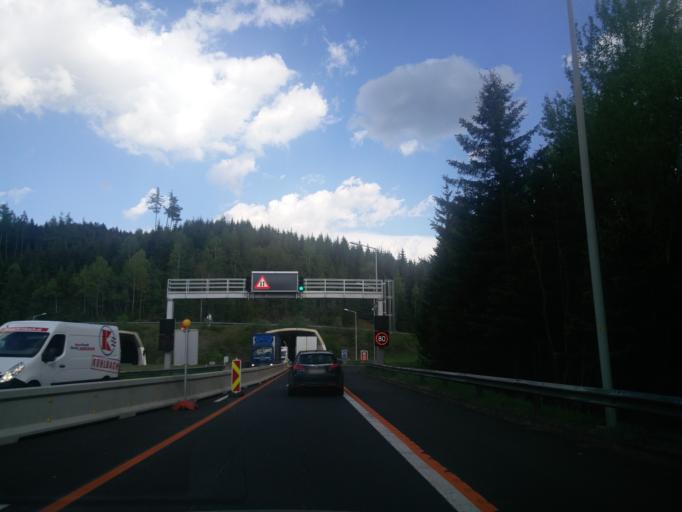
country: AT
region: Styria
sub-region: Politischer Bezirk Voitsberg
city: Pack
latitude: 46.9597
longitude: 14.9648
